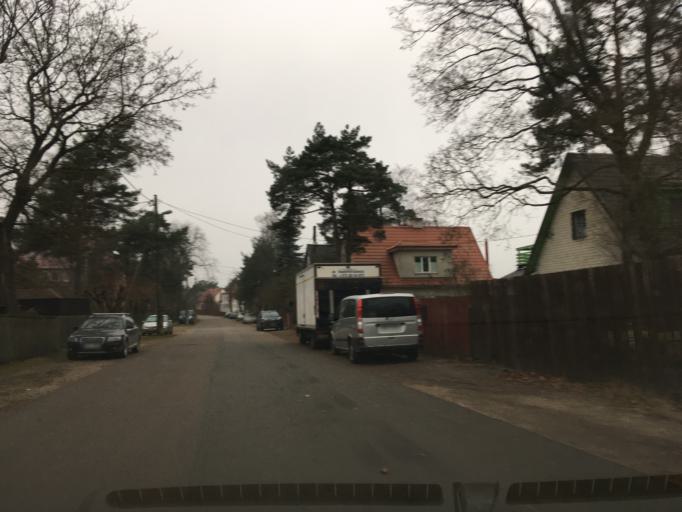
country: EE
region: Harju
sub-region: Tallinna linn
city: Tallinn
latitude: 59.4016
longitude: 24.7248
